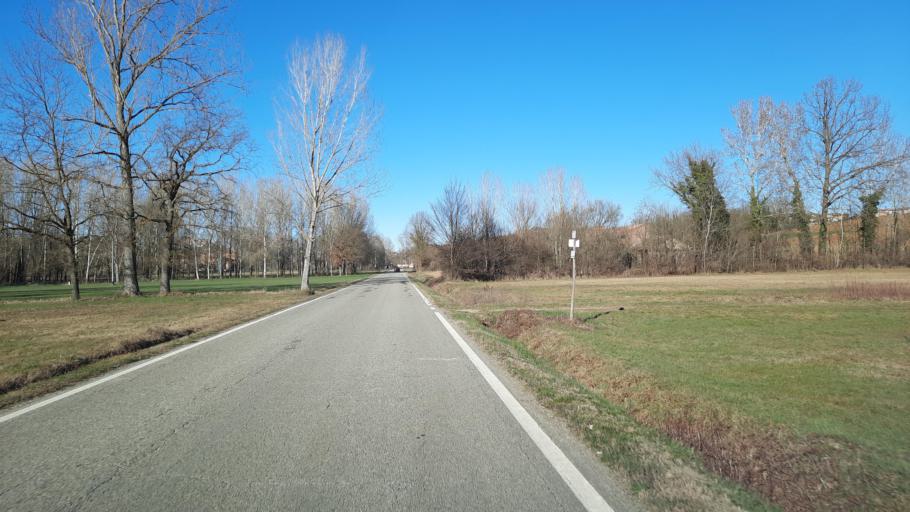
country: IT
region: Piedmont
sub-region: Provincia di Alessandria
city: Cella Monte
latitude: 45.0558
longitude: 8.3969
